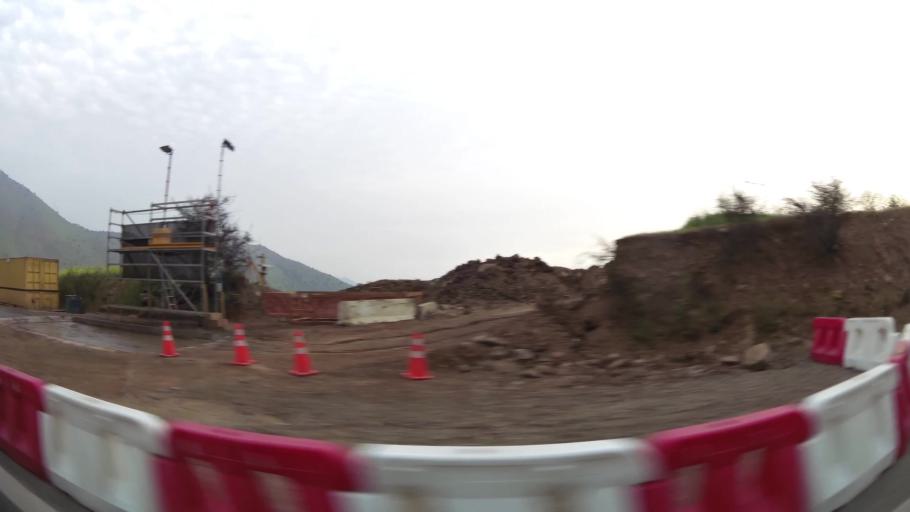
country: CL
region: Santiago Metropolitan
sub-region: Provincia de Chacabuco
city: Chicureo Abajo
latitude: -33.3516
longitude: -70.6215
